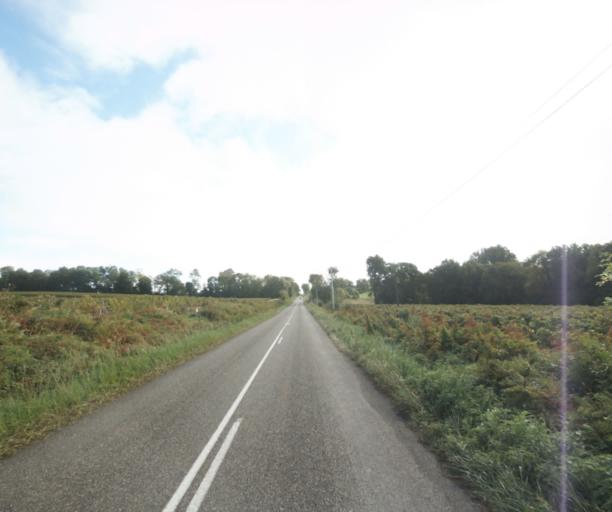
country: FR
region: Midi-Pyrenees
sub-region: Departement du Gers
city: Cazaubon
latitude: 43.8658
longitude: -0.0696
